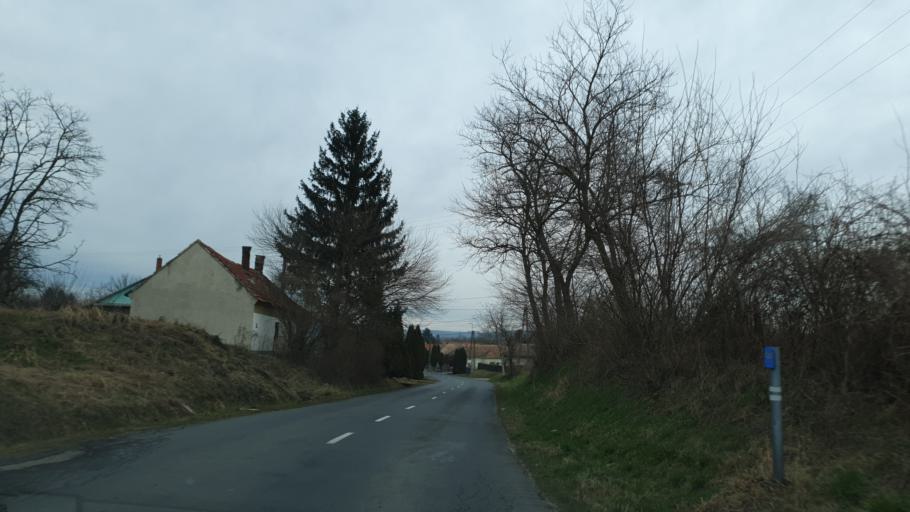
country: HU
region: Zala
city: Sarmellek
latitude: 46.7214
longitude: 17.1065
